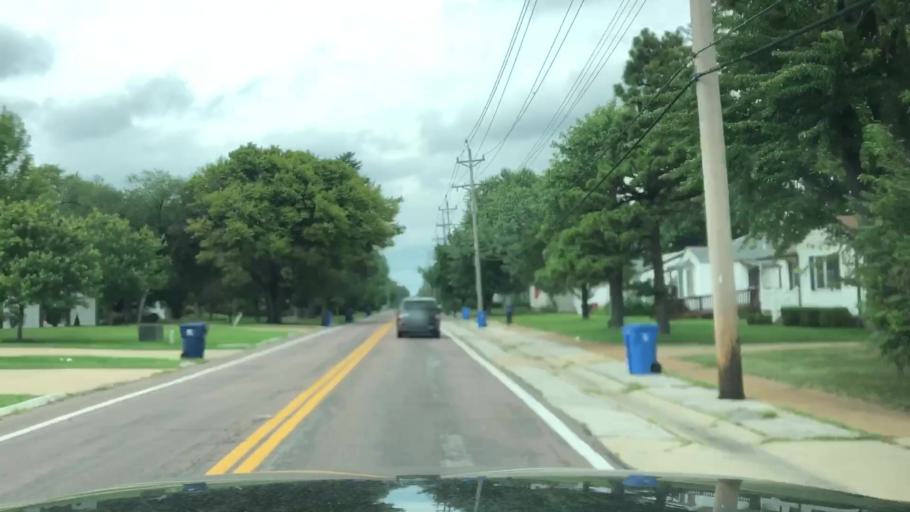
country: US
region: Missouri
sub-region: Saint Louis County
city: Florissant
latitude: 38.7986
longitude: -90.3417
